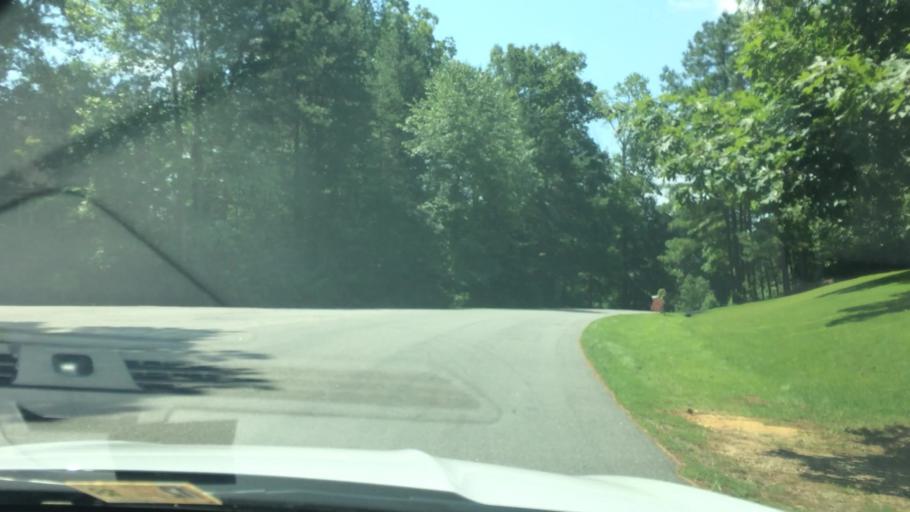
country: US
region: Virginia
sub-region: Henrico County
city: Sandston
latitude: 37.5004
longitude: -77.1706
